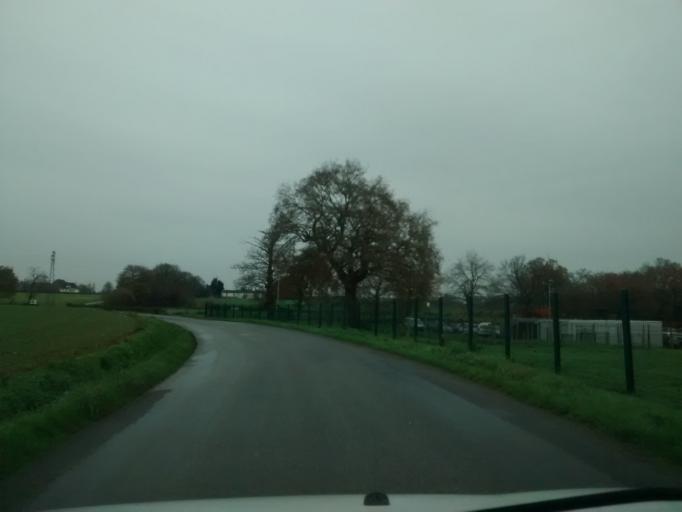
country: FR
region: Brittany
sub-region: Departement d'Ille-et-Vilaine
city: Acigne
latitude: 48.1391
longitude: -1.5470
